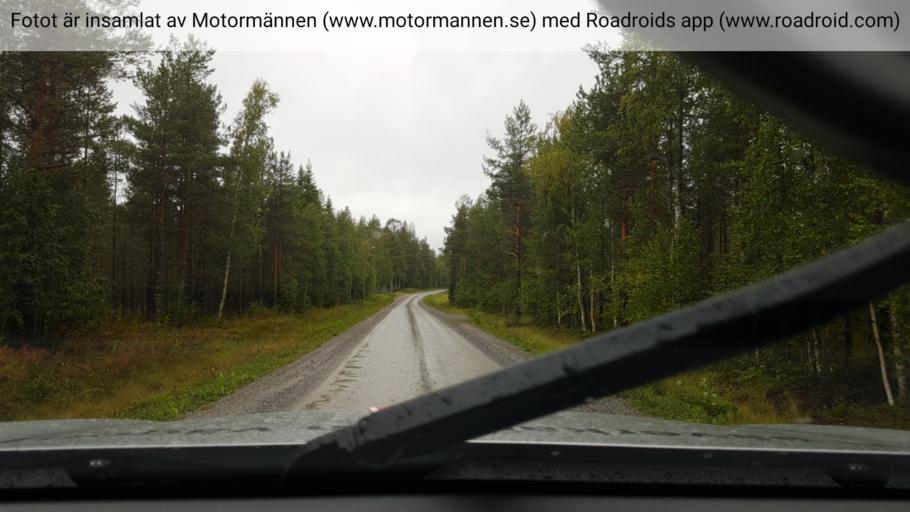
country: SE
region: Vaesterbotten
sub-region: Asele Kommun
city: Asele
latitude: 64.0195
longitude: 17.6521
